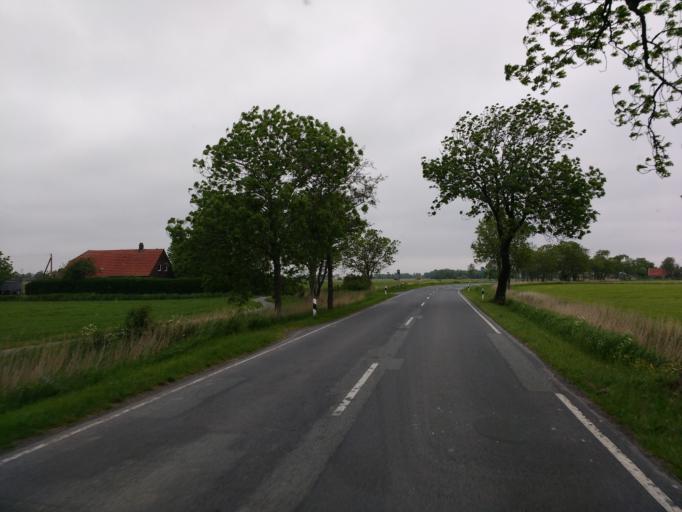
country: DE
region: Lower Saxony
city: Jever
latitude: 53.6502
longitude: 7.9195
